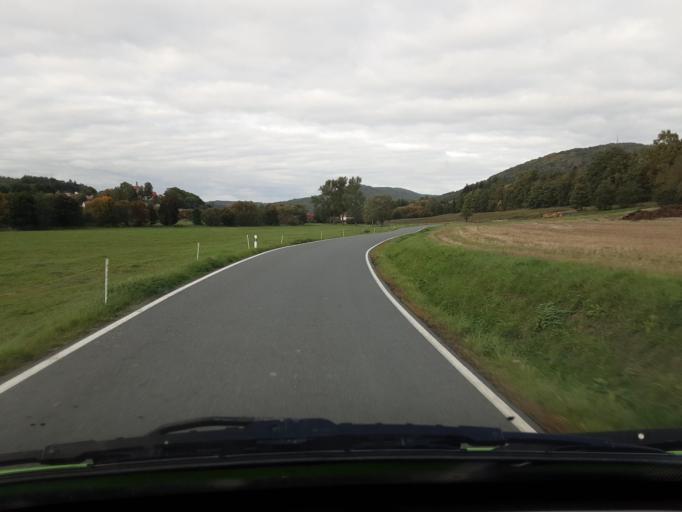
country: CZ
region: Plzensky
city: Janovice nad Uhlavou
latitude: 49.4177
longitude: 13.1766
